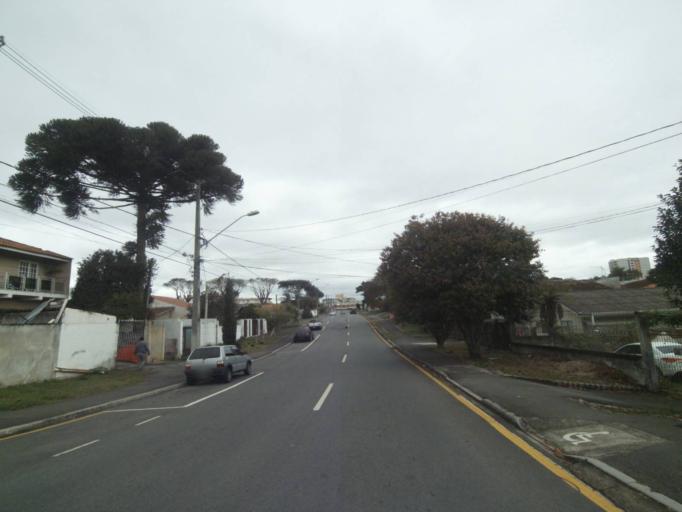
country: BR
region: Parana
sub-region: Curitiba
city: Curitiba
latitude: -25.5030
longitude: -49.2929
